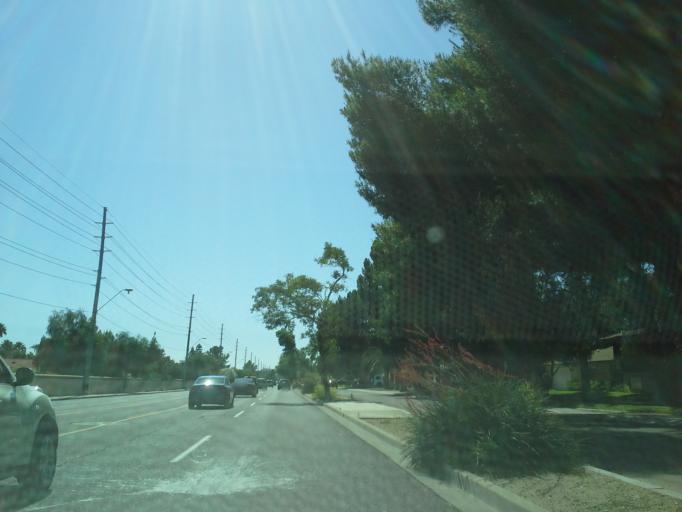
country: US
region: Arizona
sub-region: Maricopa County
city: Paradise Valley
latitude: 33.5972
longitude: -111.9650
